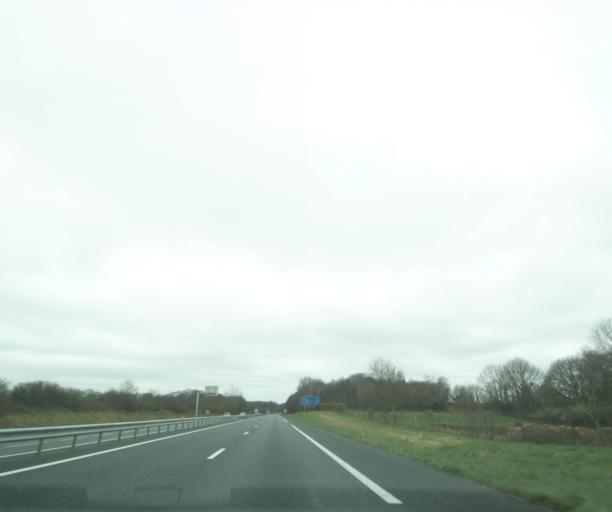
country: FR
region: Centre
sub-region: Departement de l'Indre
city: Chantome
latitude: 46.4345
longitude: 1.4786
